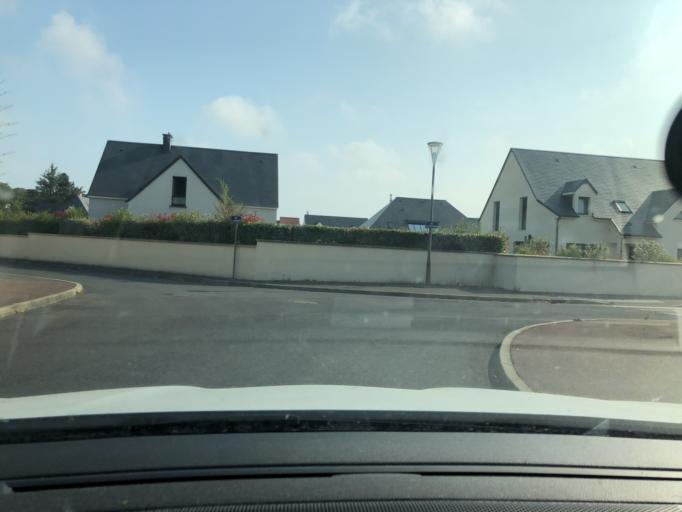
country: FR
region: Lower Normandy
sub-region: Departement du Calvados
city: Douvres-la-Delivrande
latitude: 49.2920
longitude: -0.3715
